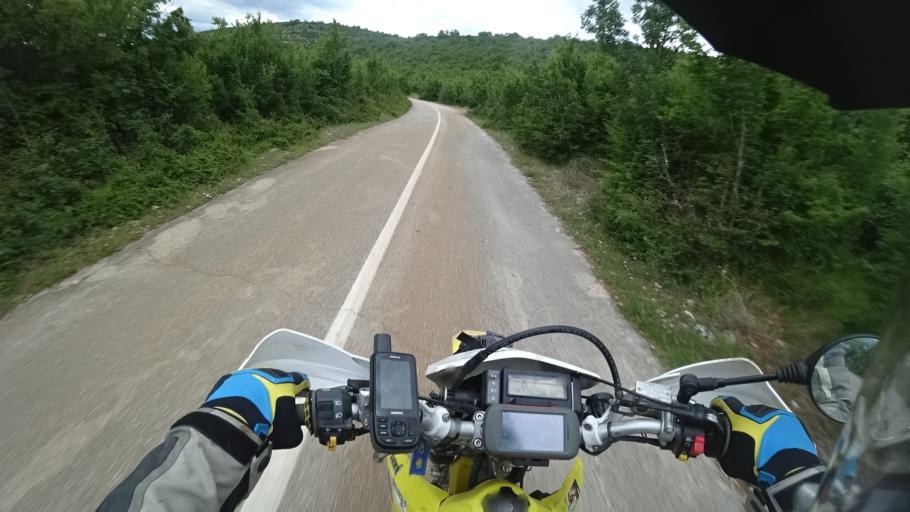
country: HR
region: Zadarska
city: Gracac
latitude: 44.1948
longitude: 15.8854
